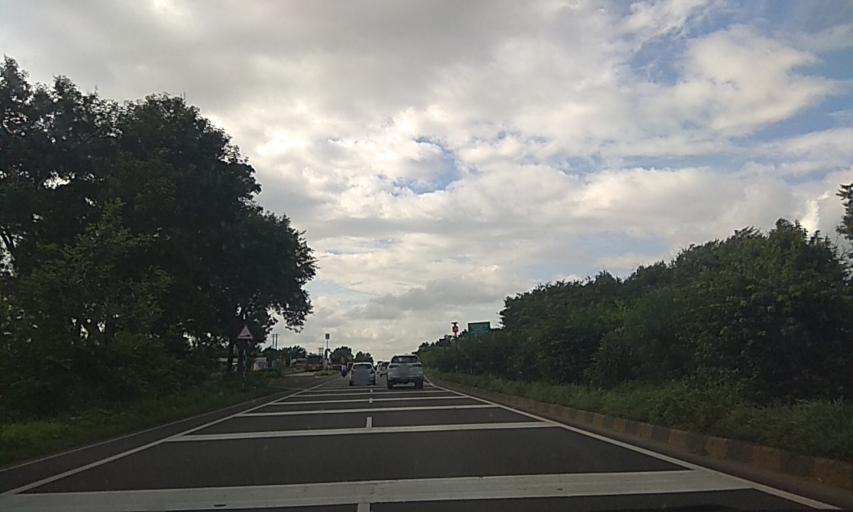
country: IN
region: Maharashtra
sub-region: Satara Division
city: Karad
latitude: 17.1146
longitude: 74.1987
